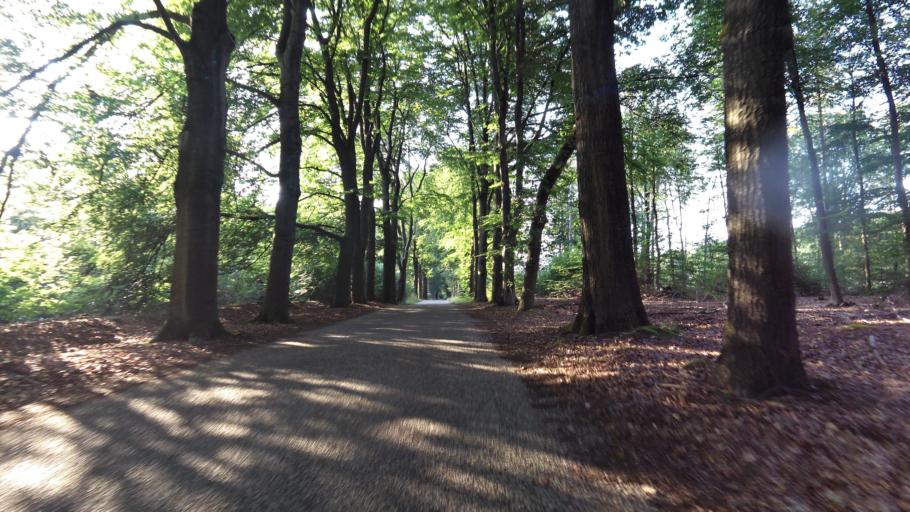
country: NL
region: Gelderland
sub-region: Gemeente Renkum
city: Oosterbeek
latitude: 52.0200
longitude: 5.8429
